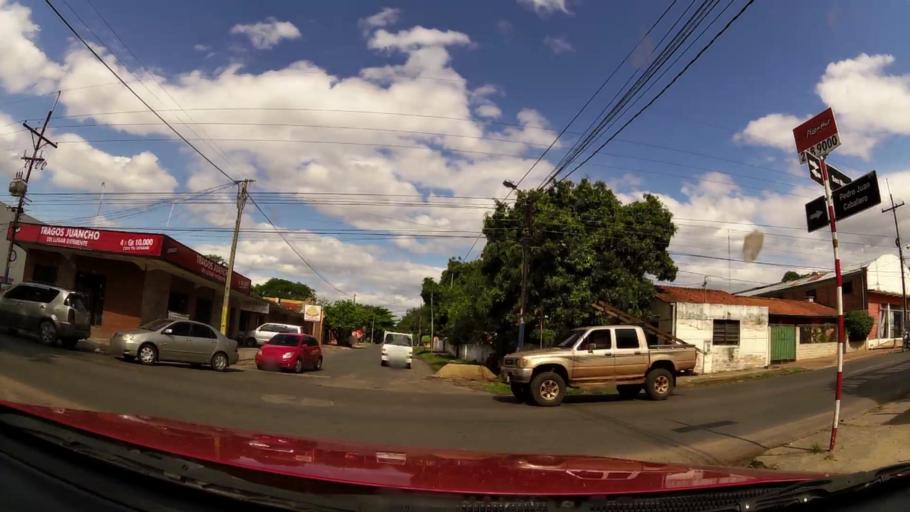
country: PY
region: Central
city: San Lorenzo
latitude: -25.2666
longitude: -57.5014
